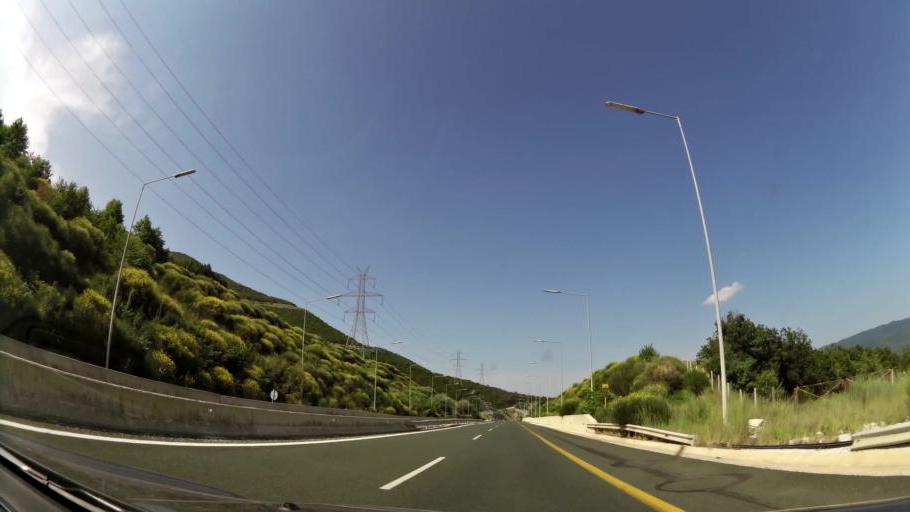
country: GR
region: Central Macedonia
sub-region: Nomos Imathias
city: Rizomata
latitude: 40.3957
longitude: 22.1606
